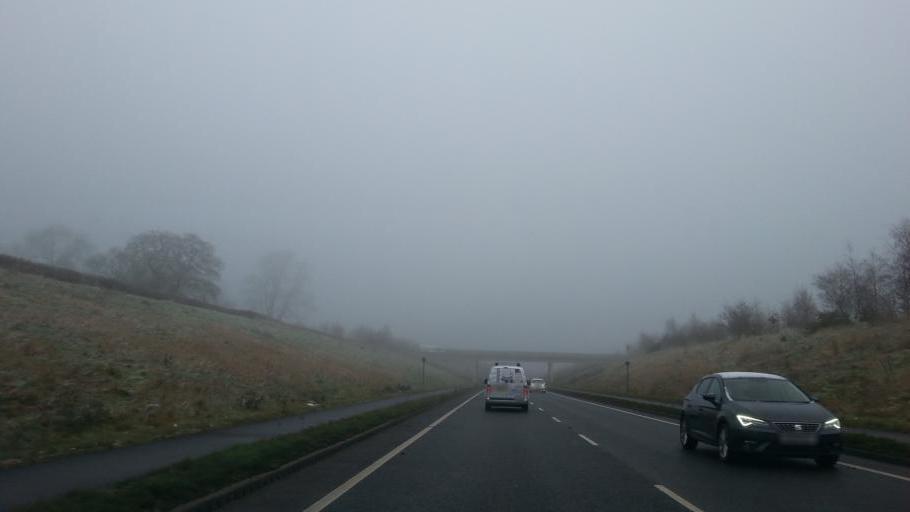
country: GB
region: England
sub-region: Cheshire East
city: Alderley Edge
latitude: 53.2982
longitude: -2.2510
